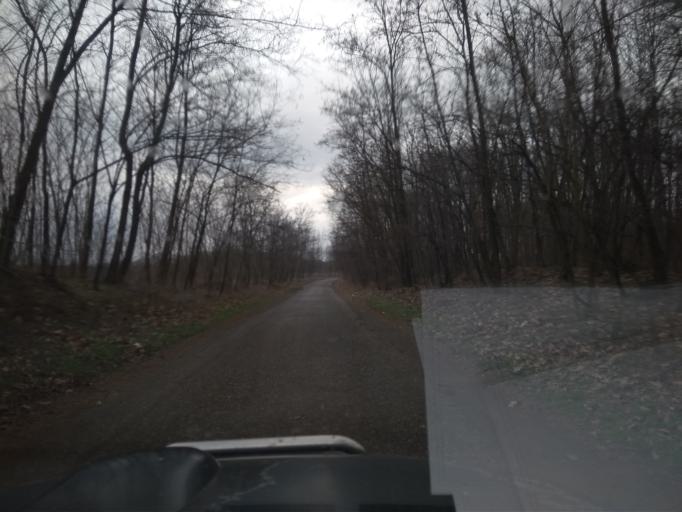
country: HU
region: Szabolcs-Szatmar-Bereg
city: Nyirpazony
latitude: 48.0158
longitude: 21.8096
